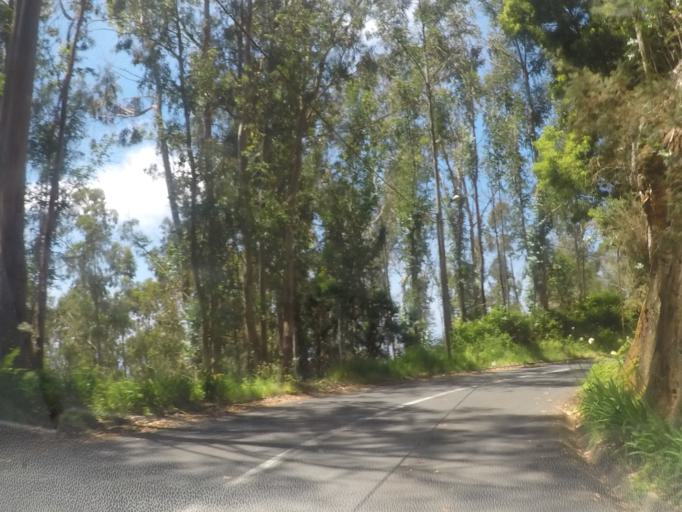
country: PT
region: Madeira
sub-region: Camara de Lobos
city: Curral das Freiras
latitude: 32.6883
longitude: -16.9755
